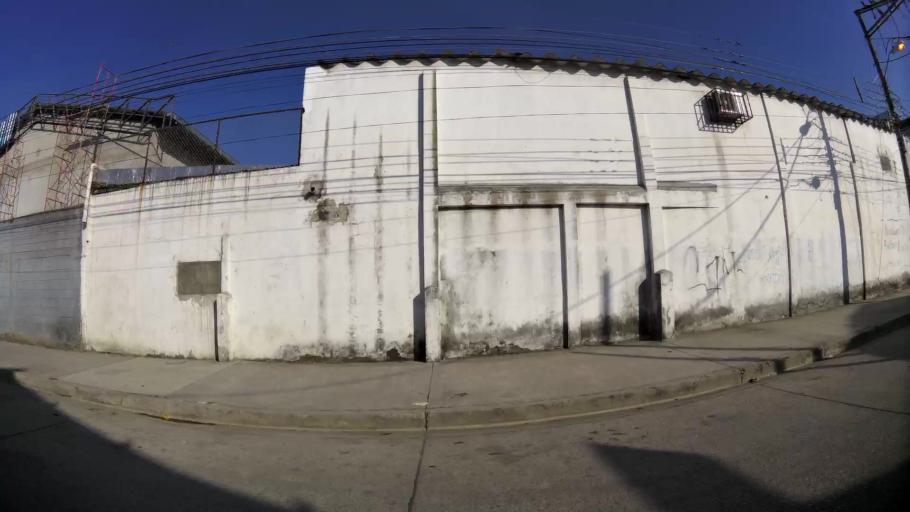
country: EC
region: Guayas
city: Guayaquil
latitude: -2.1572
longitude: -79.9284
